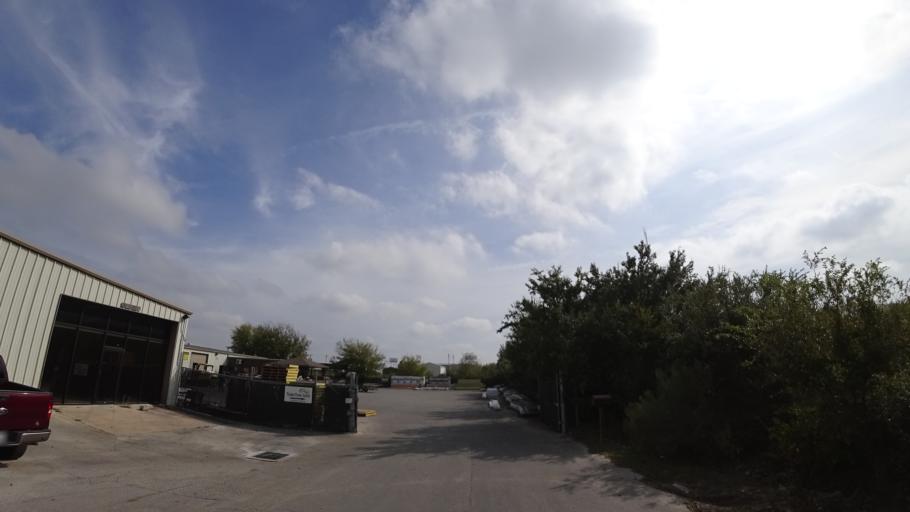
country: US
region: Texas
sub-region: Travis County
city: Wells Branch
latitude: 30.4510
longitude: -97.6648
